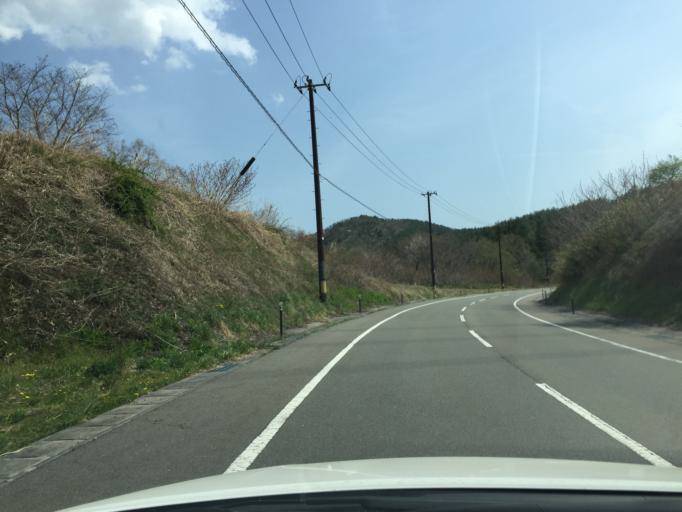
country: JP
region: Fukushima
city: Iwaki
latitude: 37.2857
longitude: 140.8425
